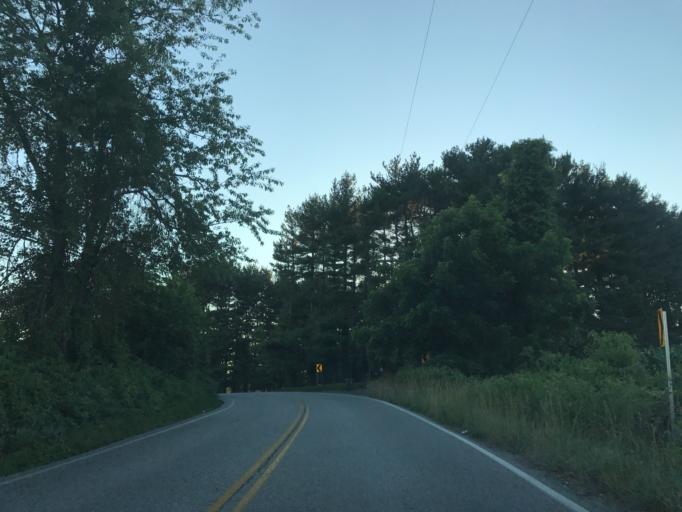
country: US
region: Maryland
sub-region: Harford County
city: Jarrettsville
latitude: 39.6019
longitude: -76.4935
